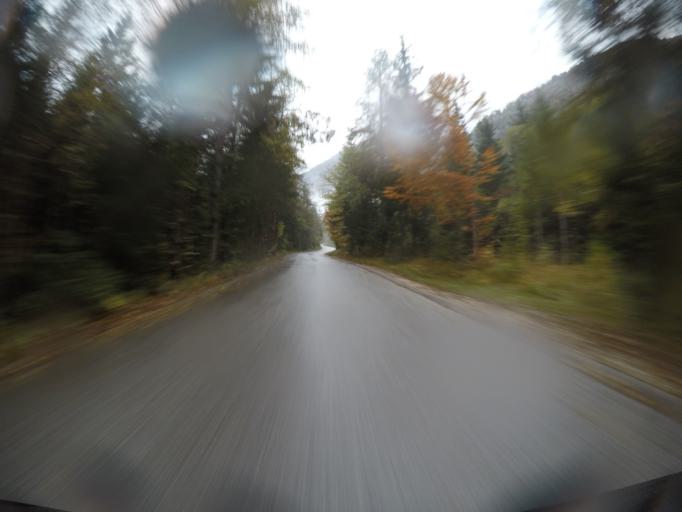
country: SI
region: Kranjska Gora
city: Kranjska Gora
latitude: 46.4074
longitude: 13.7358
